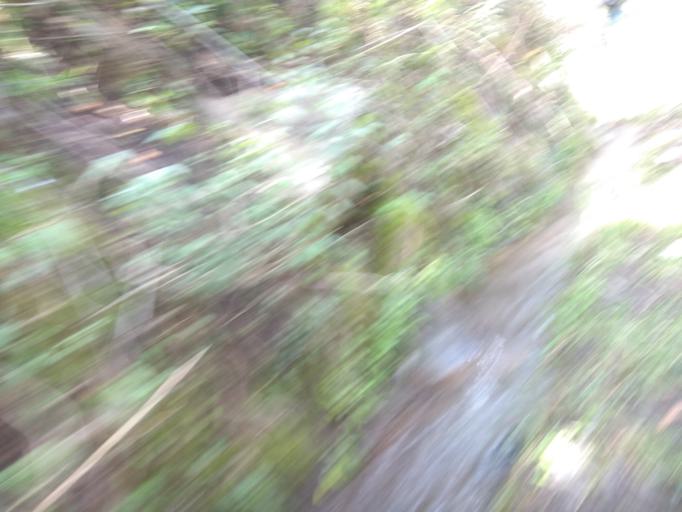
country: CO
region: Boyaca
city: Socha Viejo
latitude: 5.9798
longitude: -72.7233
